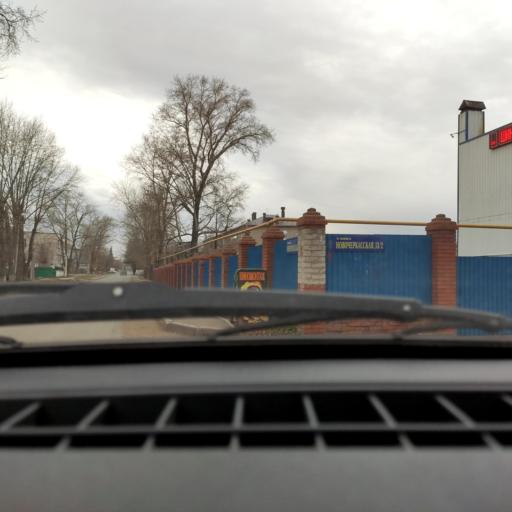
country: RU
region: Bashkortostan
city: Ufa
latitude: 54.8271
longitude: 56.0733
